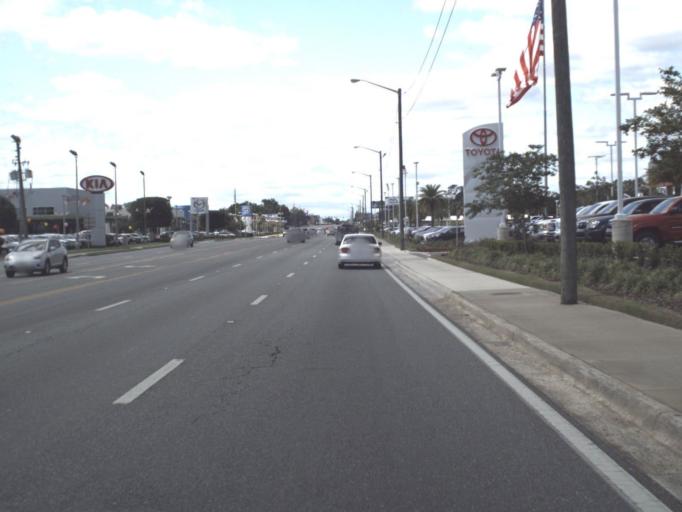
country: US
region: Florida
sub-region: Marion County
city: Ocala
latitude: 29.1782
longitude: -82.1535
